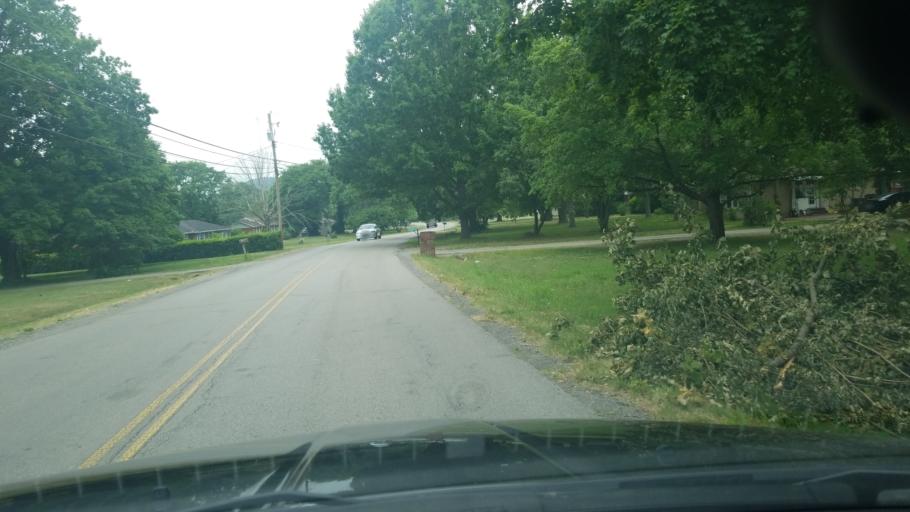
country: US
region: Tennessee
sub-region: Davidson County
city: Goodlettsville
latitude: 36.2598
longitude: -86.7606
